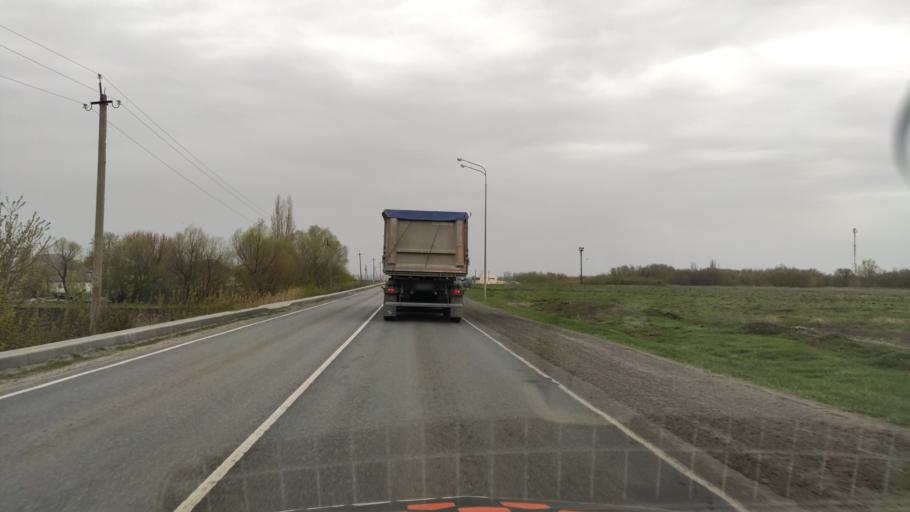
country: RU
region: Kursk
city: Gorshechnoye
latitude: 51.5293
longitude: 38.0227
